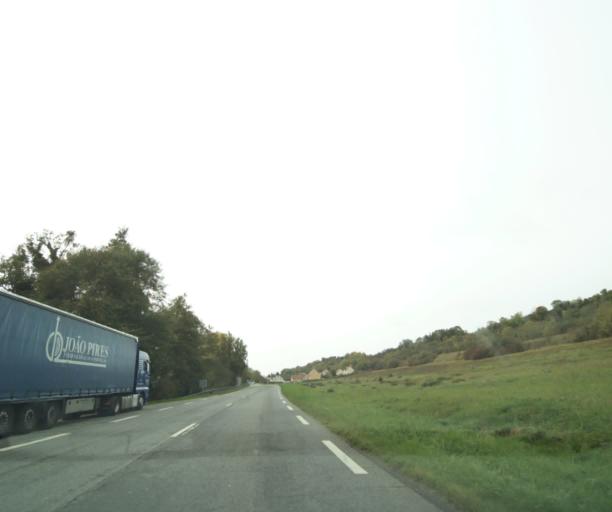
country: FR
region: Centre
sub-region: Departement d'Eure-et-Loir
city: Dreux
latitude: 48.7539
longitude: 1.3919
